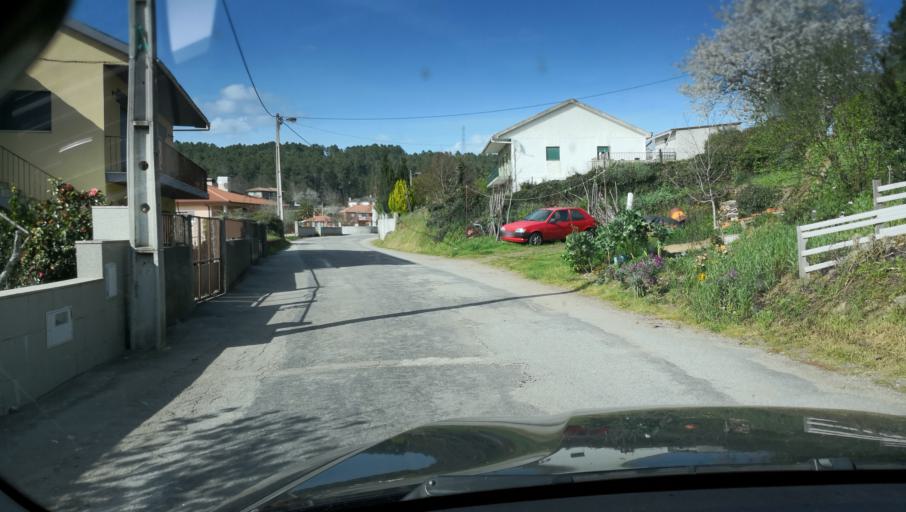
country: PT
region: Vila Real
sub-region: Sabrosa
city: Vilela
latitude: 41.2677
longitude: -7.6590
